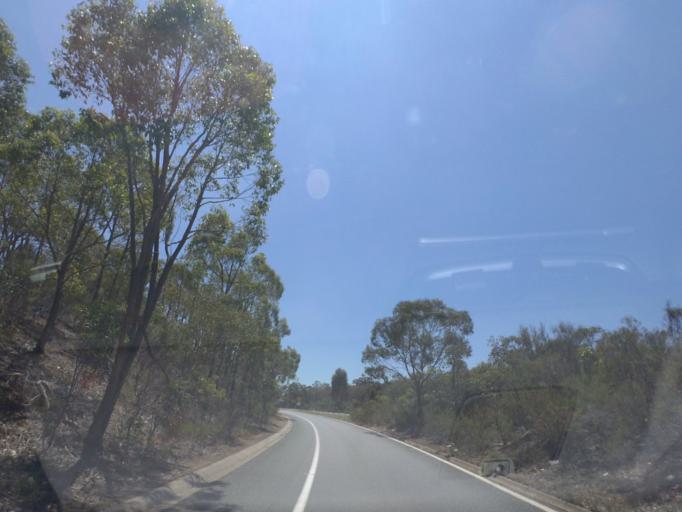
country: AU
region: Victoria
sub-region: Murrindindi
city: Kinglake West
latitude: -36.9622
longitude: 145.1827
